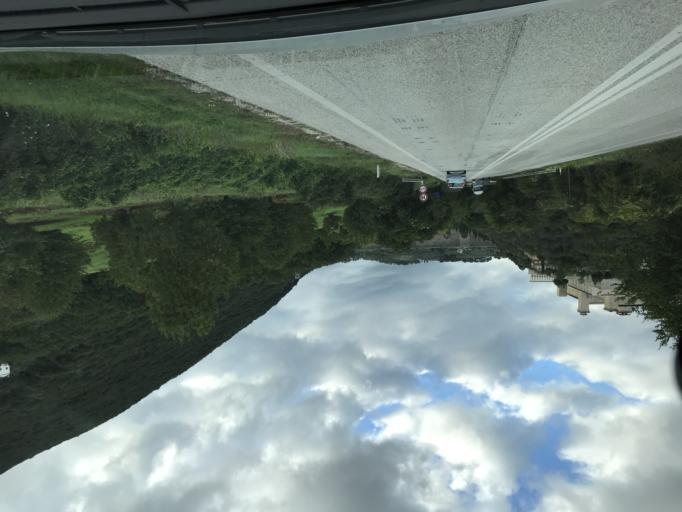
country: IT
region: Umbria
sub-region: Provincia di Perugia
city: Spoleto
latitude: 42.7292
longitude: 12.7381
